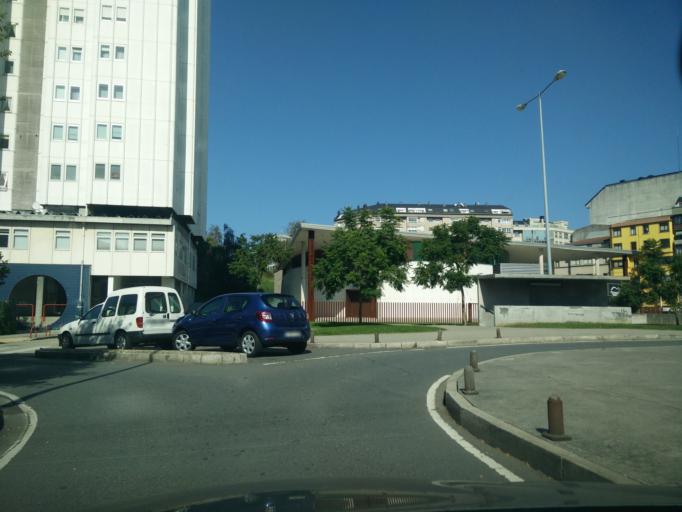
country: ES
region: Galicia
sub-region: Provincia da Coruna
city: A Coruna
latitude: 43.3506
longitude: -8.4059
